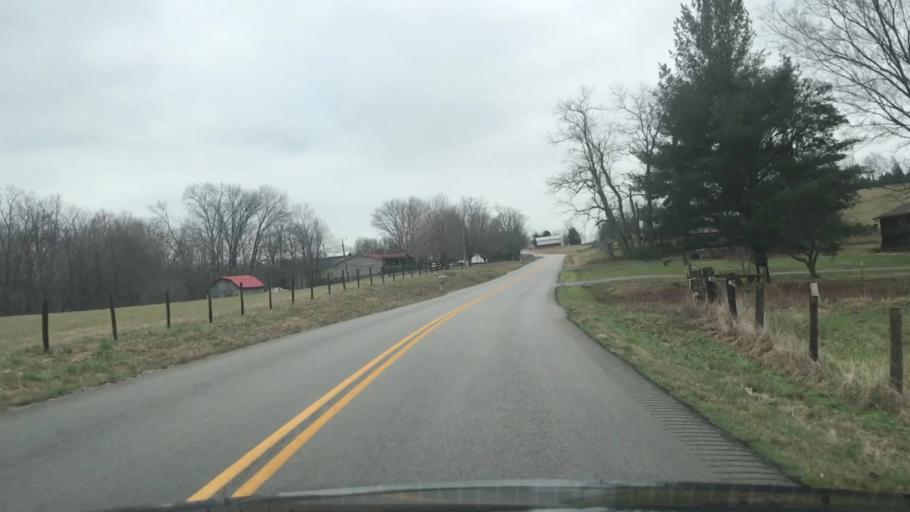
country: US
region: Kentucky
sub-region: Barren County
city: Glasgow
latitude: 36.9103
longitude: -85.7989
